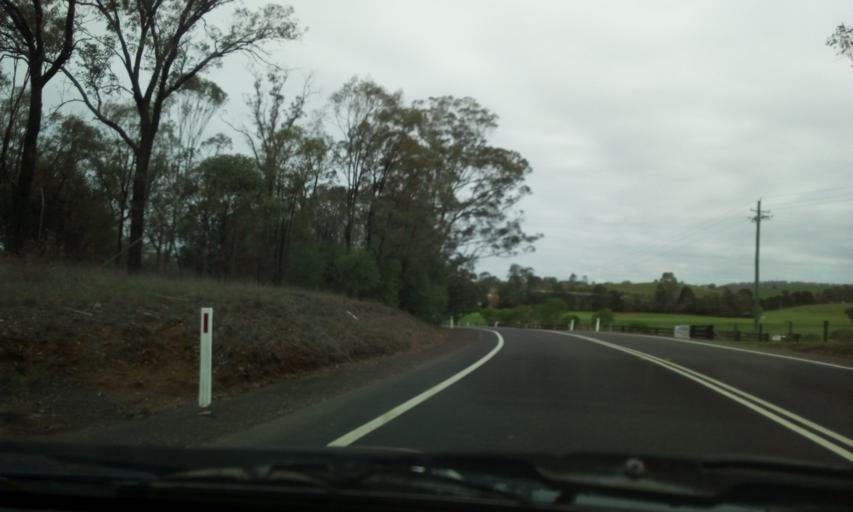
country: AU
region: New South Wales
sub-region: Camden
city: Camden South
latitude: -34.1242
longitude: 150.6997
